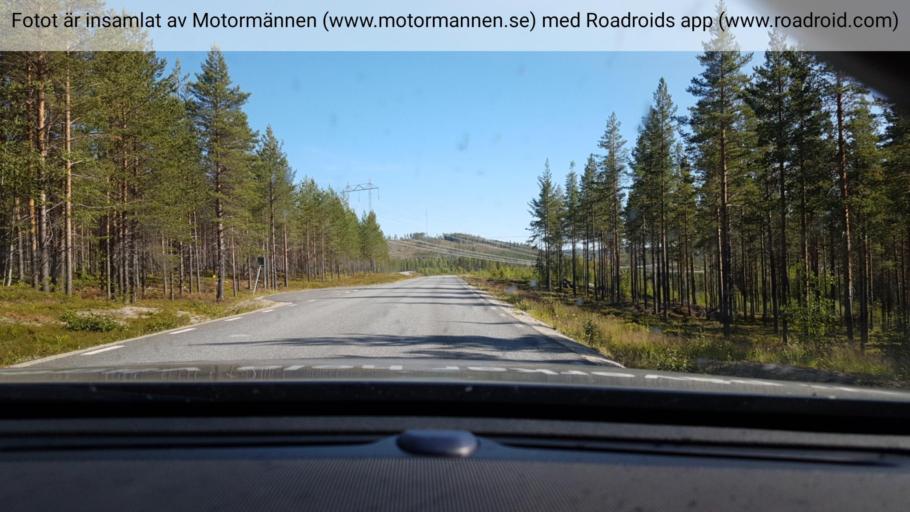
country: SE
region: Vaesterbotten
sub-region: Lycksele Kommun
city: Lycksele
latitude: 64.4852
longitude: 18.8985
